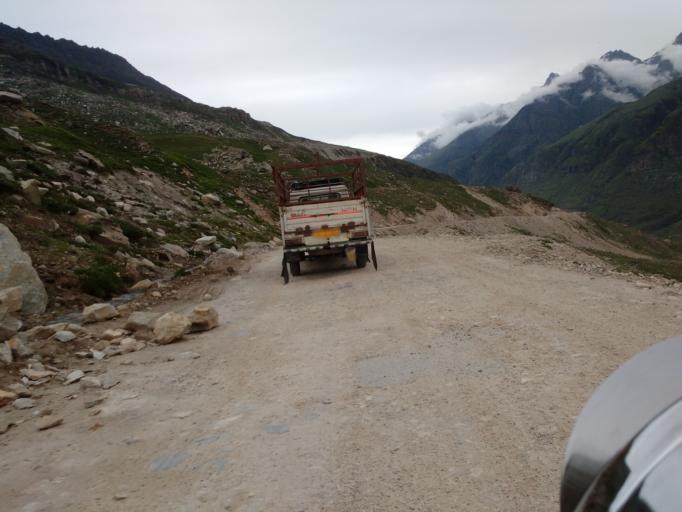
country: IN
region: Himachal Pradesh
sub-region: Kulu
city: Manali
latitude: 32.3806
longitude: 77.2656
